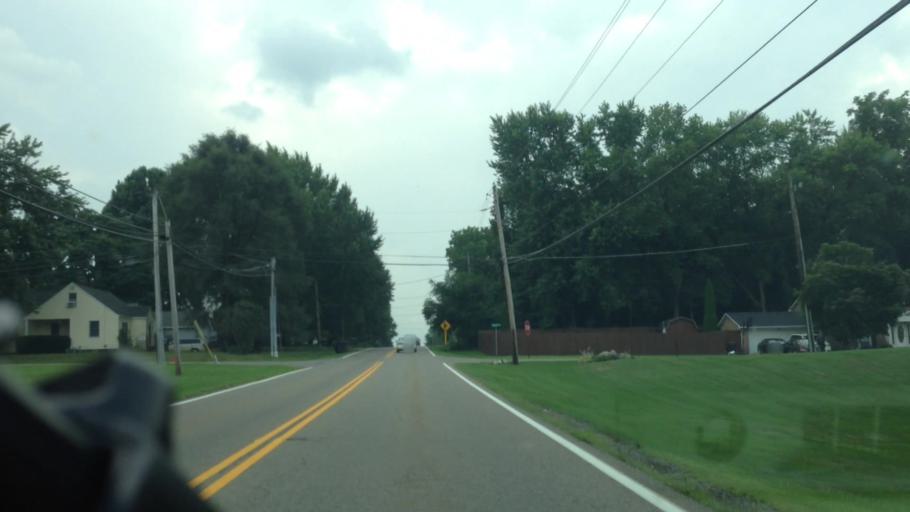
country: US
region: Ohio
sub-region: Stark County
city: Massillon
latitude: 40.8288
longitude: -81.5125
